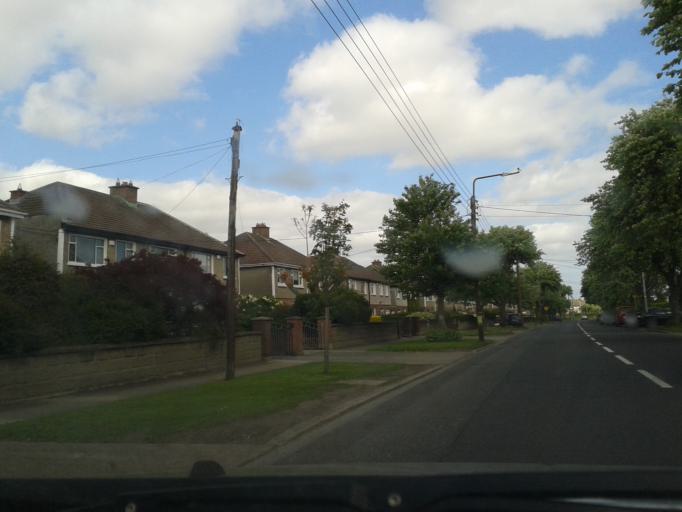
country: IE
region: Leinster
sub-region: Dublin City
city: Finglas
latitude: 53.3907
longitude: -6.2840
